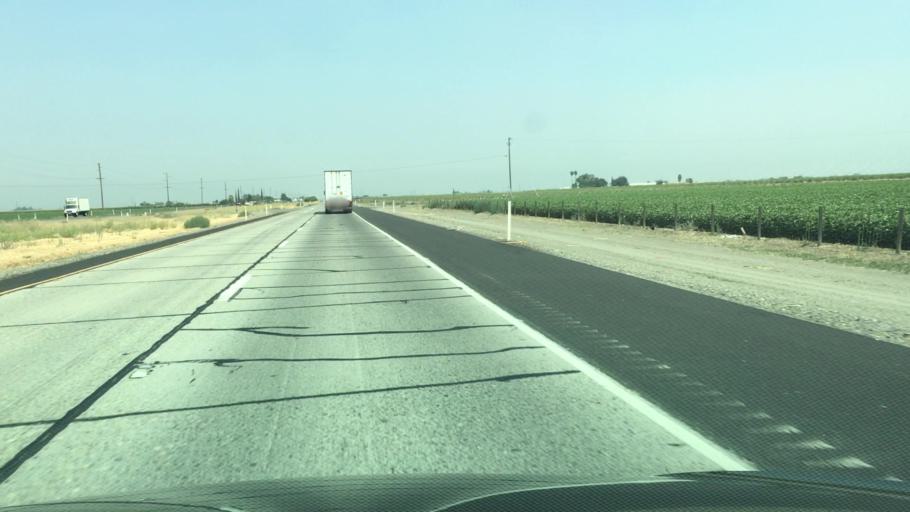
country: US
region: California
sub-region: Merced County
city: South Dos Palos
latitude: 37.0546
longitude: -120.7279
